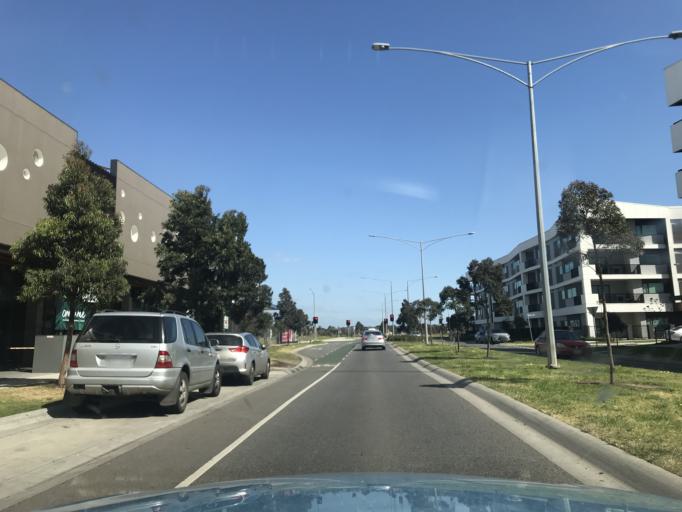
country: AU
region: Victoria
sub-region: Wyndham
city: Williams Landing
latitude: -37.8667
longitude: 144.7429
